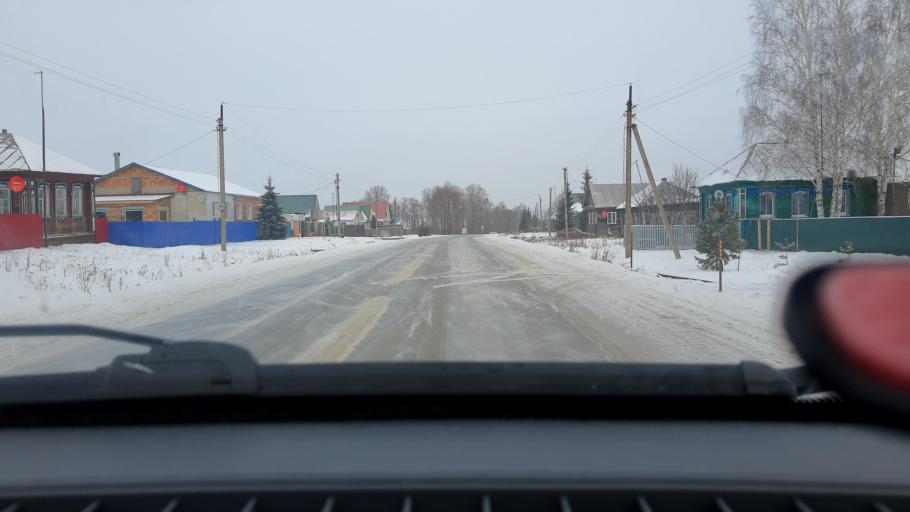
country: RU
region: Bashkortostan
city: Iglino
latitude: 54.7382
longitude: 56.3967
